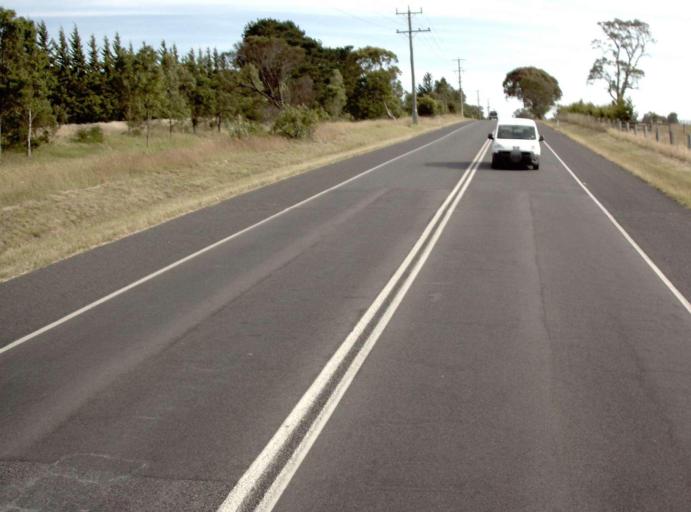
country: AU
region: Victoria
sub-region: Latrobe
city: Traralgon
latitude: -38.1762
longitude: 146.5635
